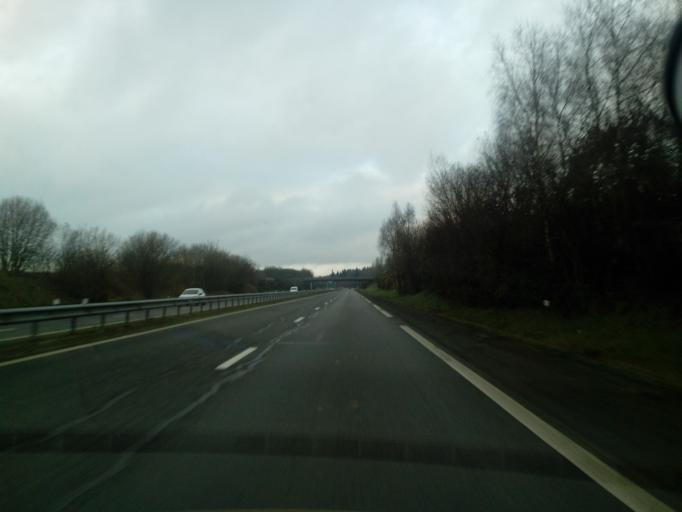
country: FR
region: Brittany
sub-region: Departement d'Ille-et-Vilaine
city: Saint-Meen-le-Grand
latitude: 48.1859
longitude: -2.2093
